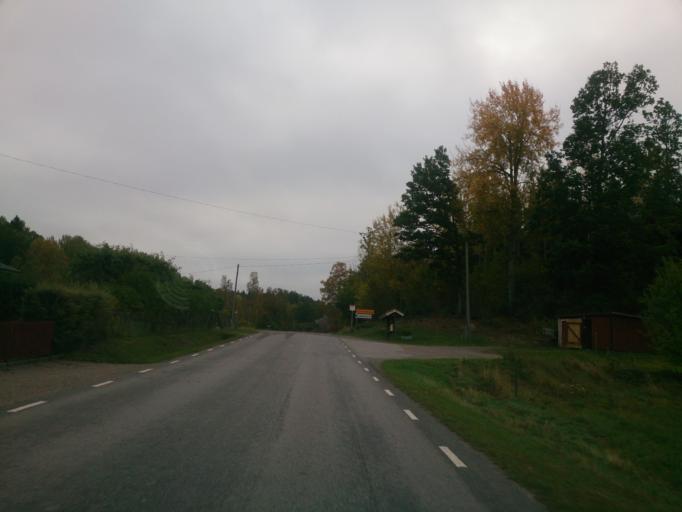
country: SE
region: OEstergoetland
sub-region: Atvidabergs Kommun
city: Atvidaberg
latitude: 58.1813
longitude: 16.0565
